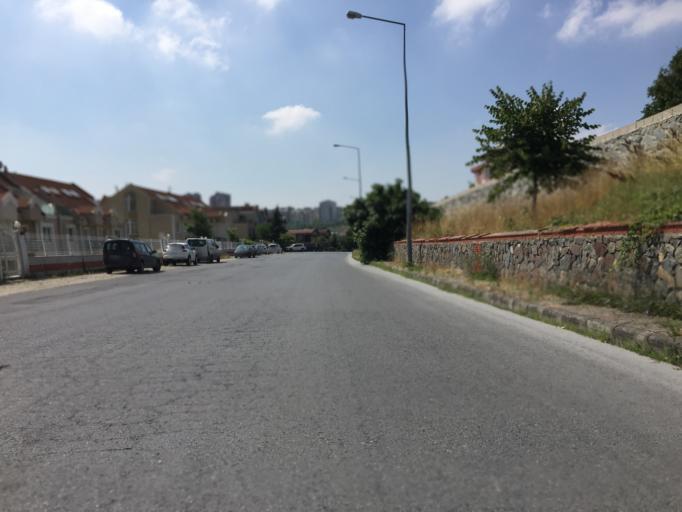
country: TR
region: Istanbul
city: Esenyurt
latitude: 41.0839
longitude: 28.6611
